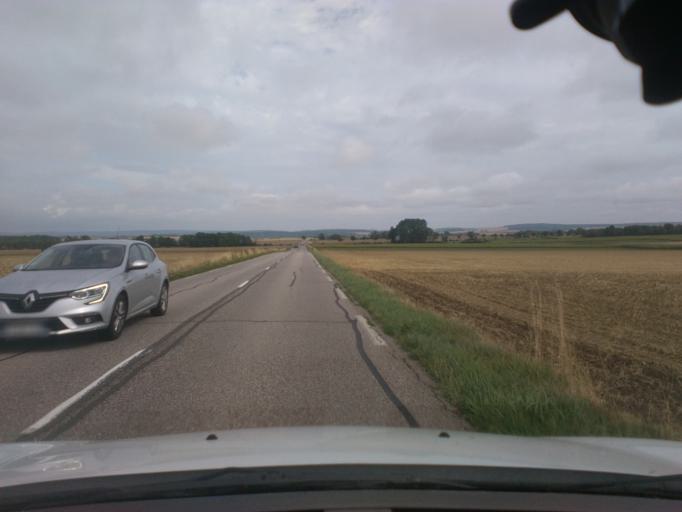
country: FR
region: Lorraine
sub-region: Departement de Meurthe-et-Moselle
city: Vezelise
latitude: 48.4815
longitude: 6.1422
